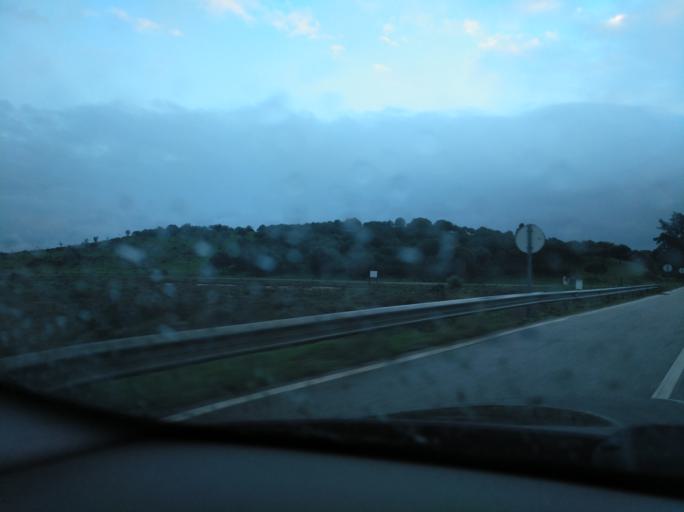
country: PT
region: Faro
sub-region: Castro Marim
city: Castro Marim
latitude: 37.2145
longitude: -7.4705
